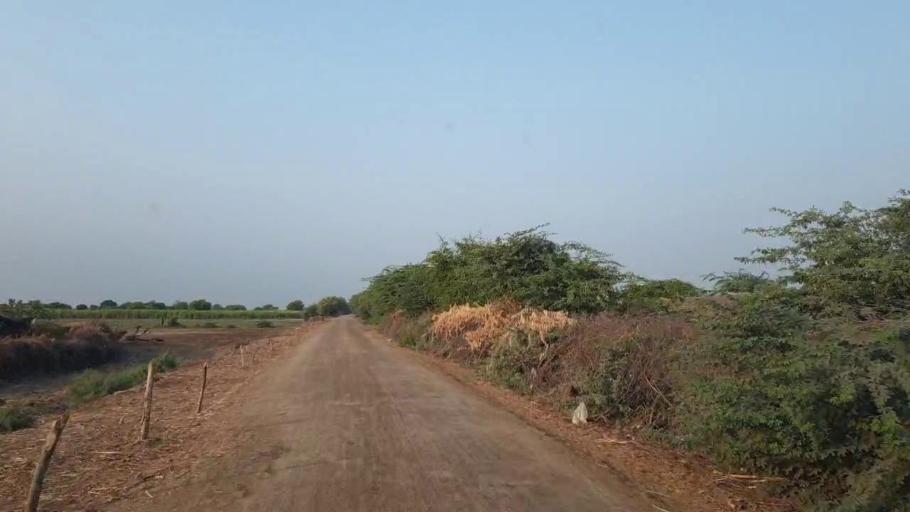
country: PK
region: Sindh
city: Rajo Khanani
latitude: 25.0389
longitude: 68.9643
